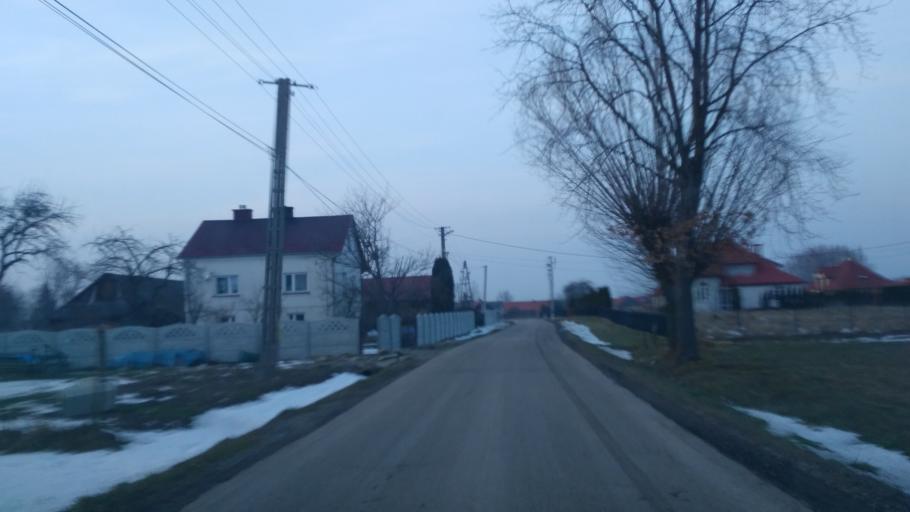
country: PL
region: Subcarpathian Voivodeship
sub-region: Powiat rzeszowski
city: Siedliska
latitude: 49.9703
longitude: 21.9651
